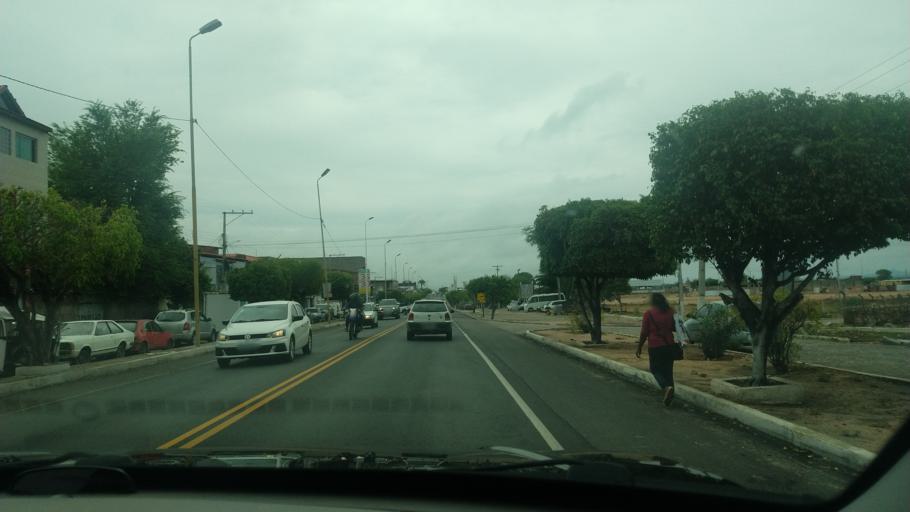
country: BR
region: Bahia
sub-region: Paulo Afonso
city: Paulo Afonso
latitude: -9.4047
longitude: -38.2380
